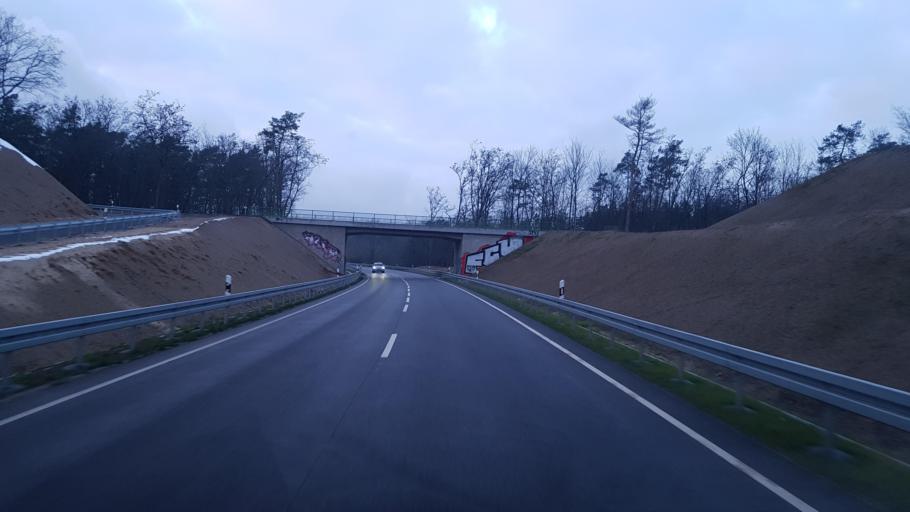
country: DE
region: Brandenburg
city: Wildau
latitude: 52.3219
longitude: 13.6570
